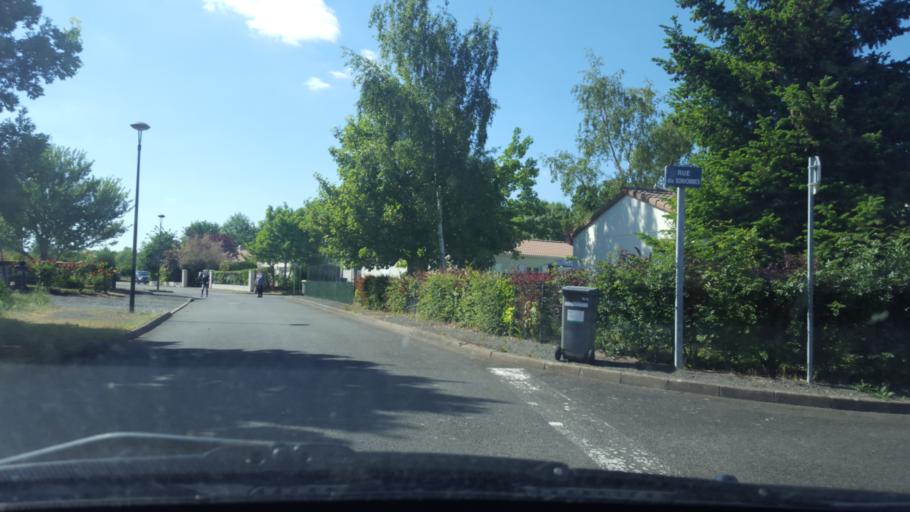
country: FR
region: Pays de la Loire
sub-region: Departement de la Loire-Atlantique
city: Saint-Philbert-de-Grand-Lieu
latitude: 47.0414
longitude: -1.6479
